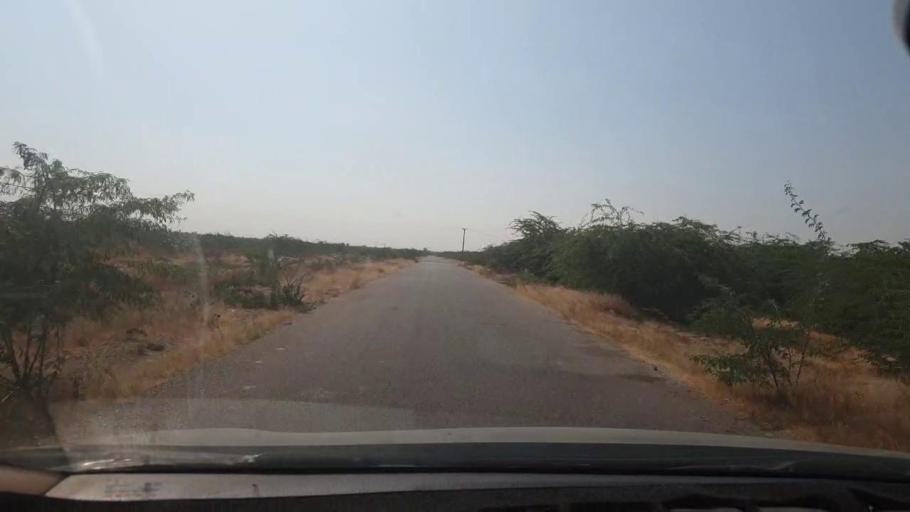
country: PK
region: Sindh
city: Malir Cantonment
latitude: 25.1616
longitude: 67.1515
